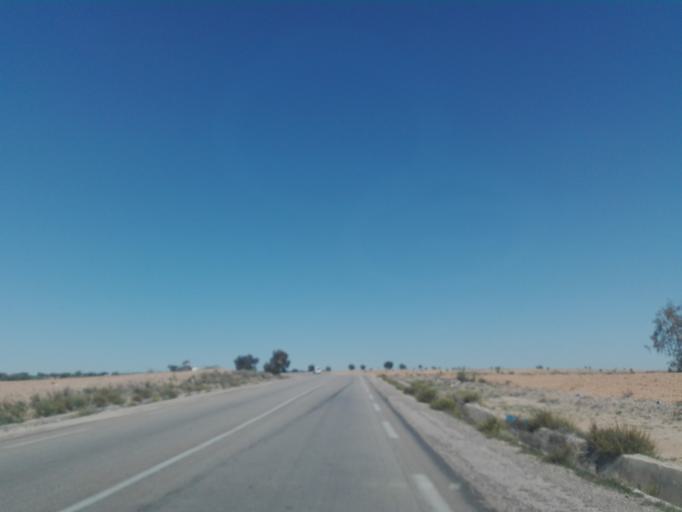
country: TN
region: Safaqis
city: Bi'r `Ali Bin Khalifah
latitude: 34.7455
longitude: 10.3619
